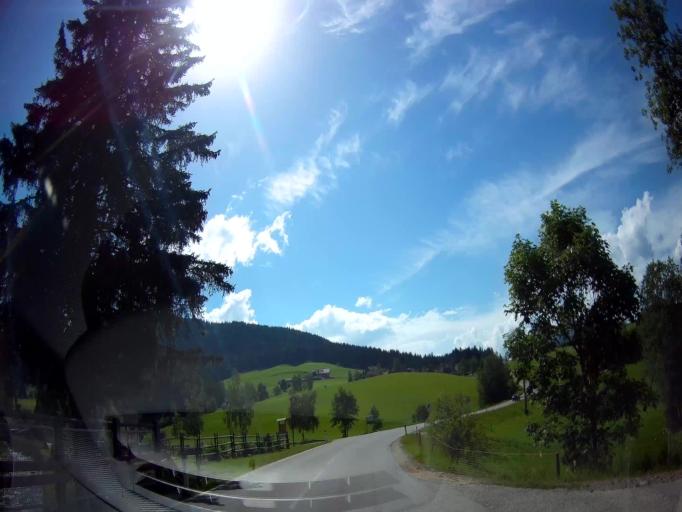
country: AT
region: Salzburg
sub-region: Politischer Bezirk Tamsweg
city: Thomatal
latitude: 47.0788
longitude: 13.7324
